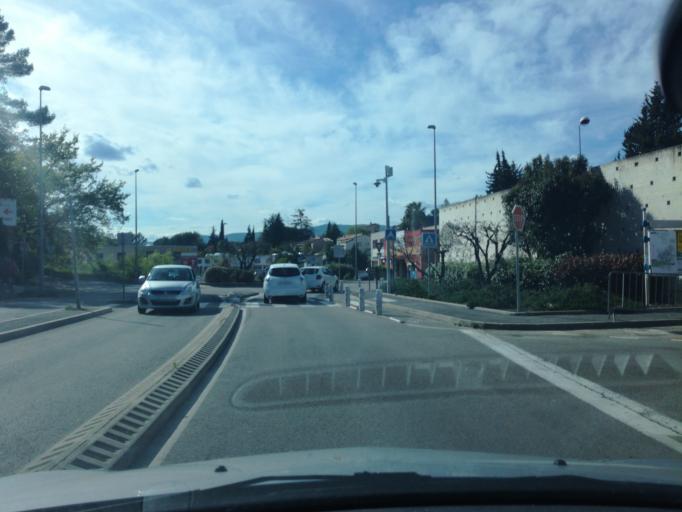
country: FR
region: Provence-Alpes-Cote d'Azur
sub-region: Departement des Alpes-Maritimes
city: Mouans-Sartoux
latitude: 43.6137
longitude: 6.9675
